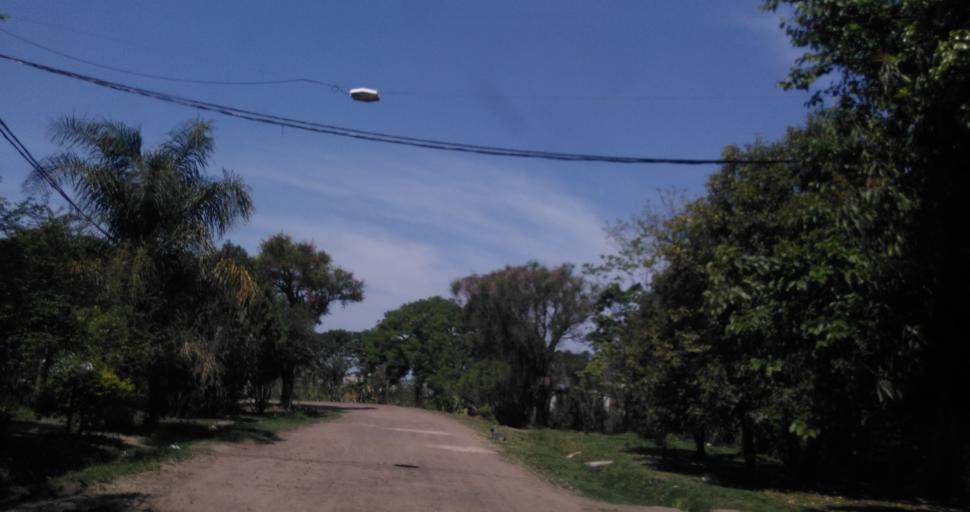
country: AR
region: Chaco
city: Fontana
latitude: -27.4036
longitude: -59.0023
